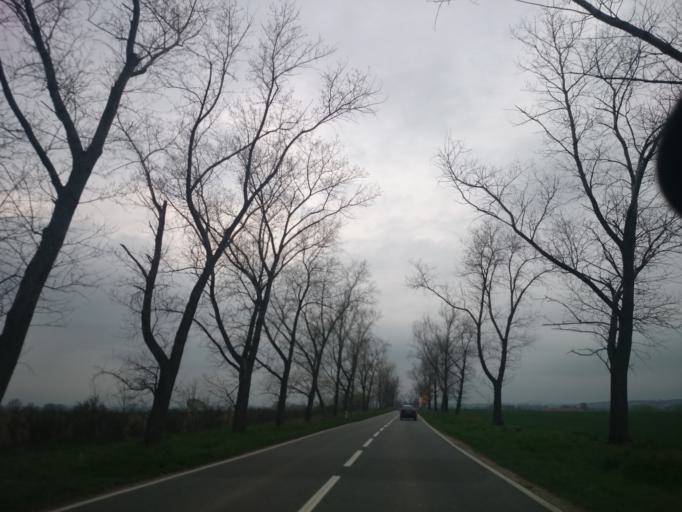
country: PL
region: Lower Silesian Voivodeship
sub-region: Powiat zabkowicki
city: Kamieniec Zabkowicki
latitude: 50.5533
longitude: 16.8561
